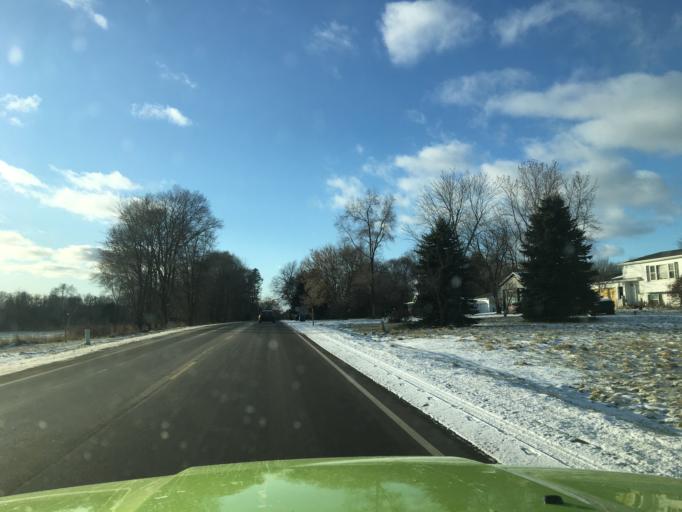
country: US
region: Michigan
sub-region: Montcalm County
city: Greenville
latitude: 43.2064
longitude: -85.2601
